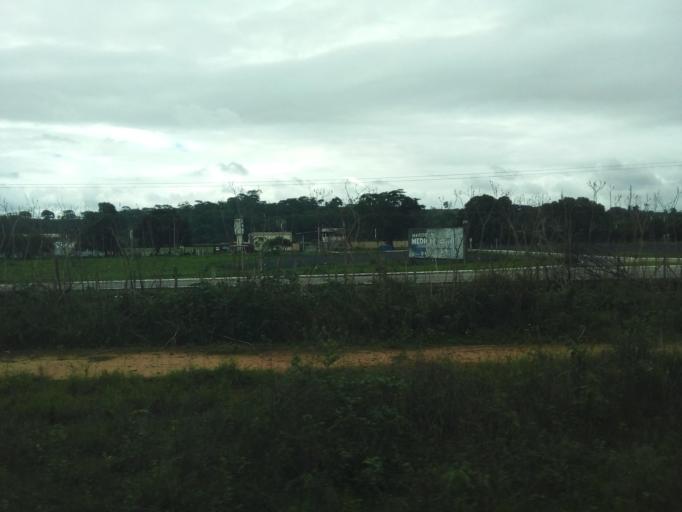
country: BR
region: Minas Gerais
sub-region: Ipatinga
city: Ipatinga
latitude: -19.4761
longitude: -42.4866
